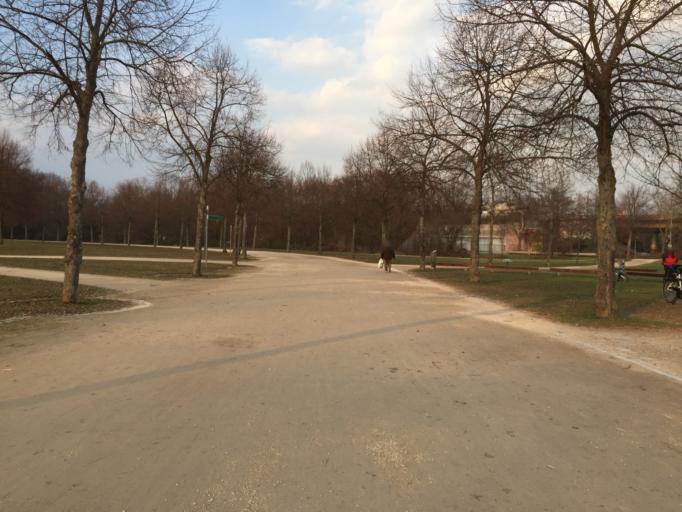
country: DE
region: Hesse
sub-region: Regierungsbezirk Darmstadt
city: Frankfurt am Main
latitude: 50.1424
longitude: 8.6409
